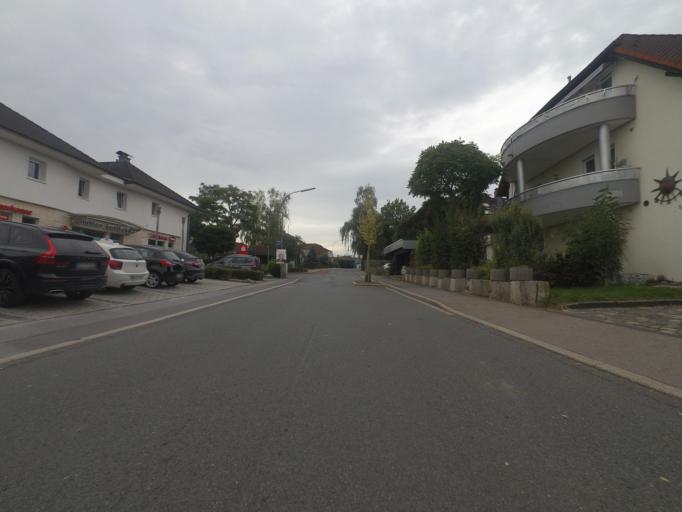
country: DE
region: North Rhine-Westphalia
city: Iserlohn
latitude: 51.4222
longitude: 7.6704
